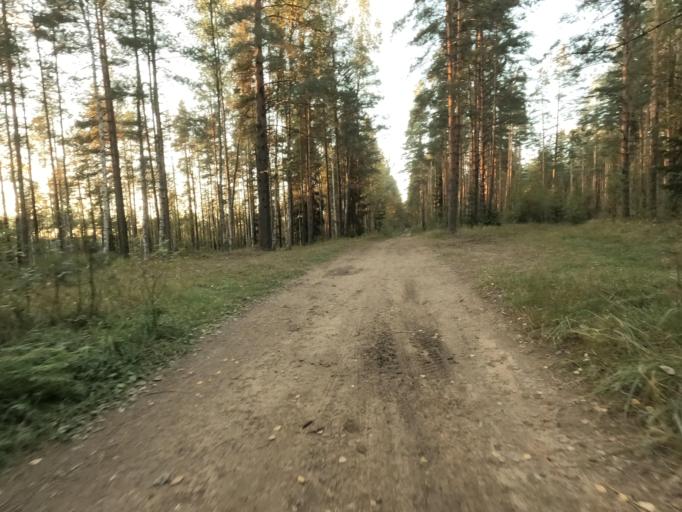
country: RU
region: Leningrad
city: Otradnoye
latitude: 59.8404
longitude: 30.8033
